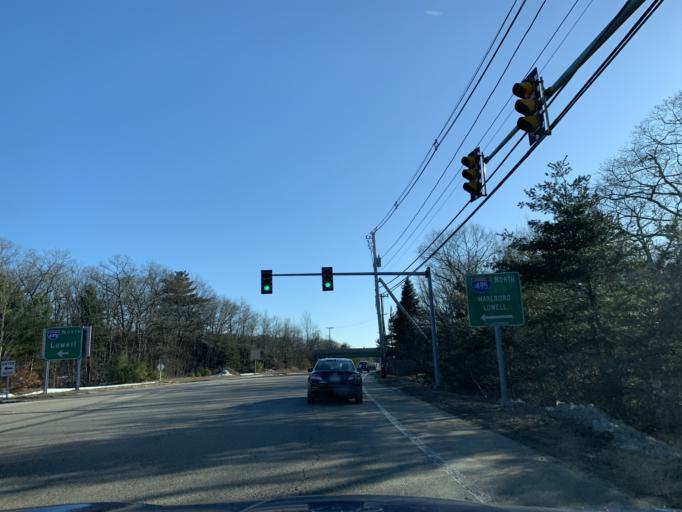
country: US
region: Massachusetts
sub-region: Norfolk County
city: Wrentham
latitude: 42.0419
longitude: -71.3441
